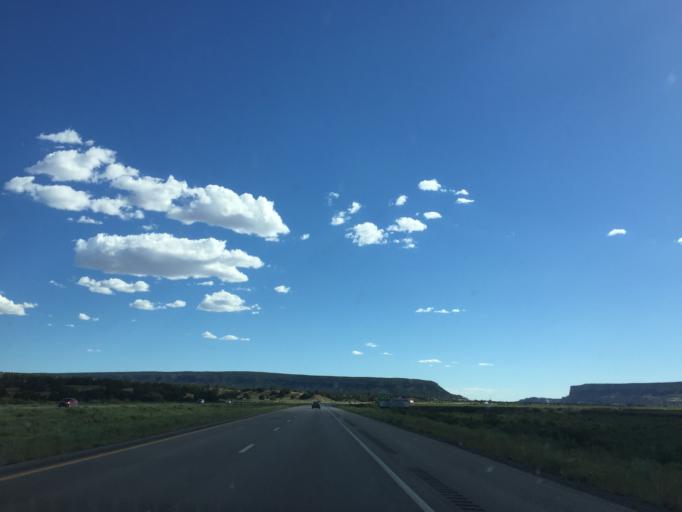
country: US
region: Arizona
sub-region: Apache County
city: Houck
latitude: 35.3904
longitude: -109.0102
